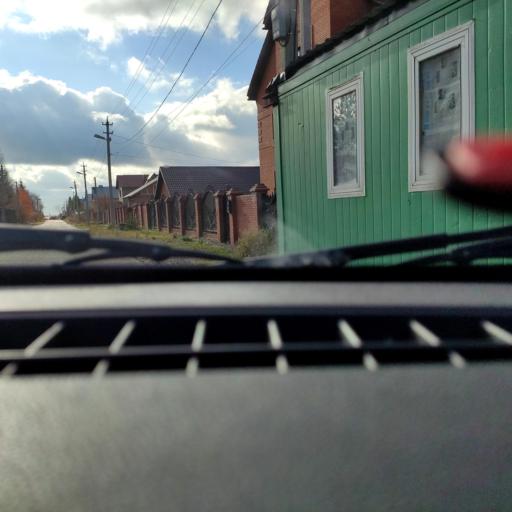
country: RU
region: Bashkortostan
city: Ufa
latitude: 54.5985
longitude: 55.9340
